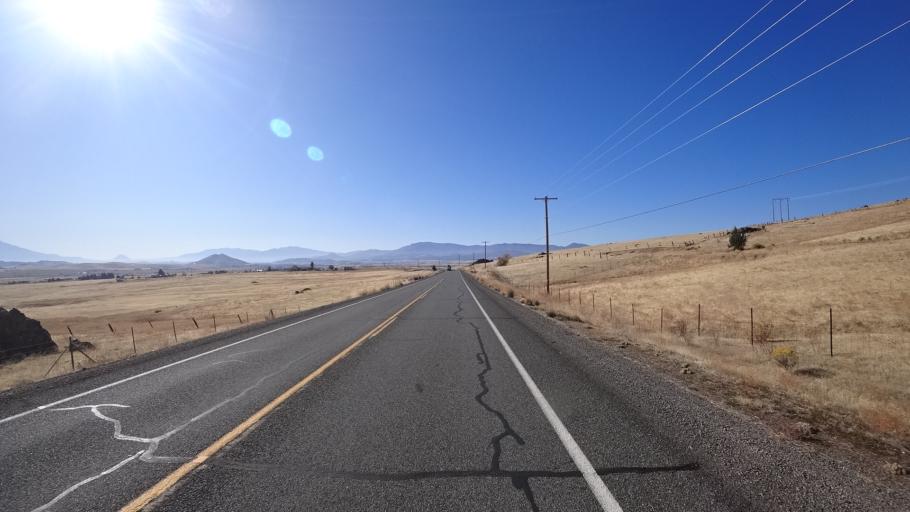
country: US
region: California
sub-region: Siskiyou County
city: Montague
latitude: 41.7785
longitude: -122.5224
